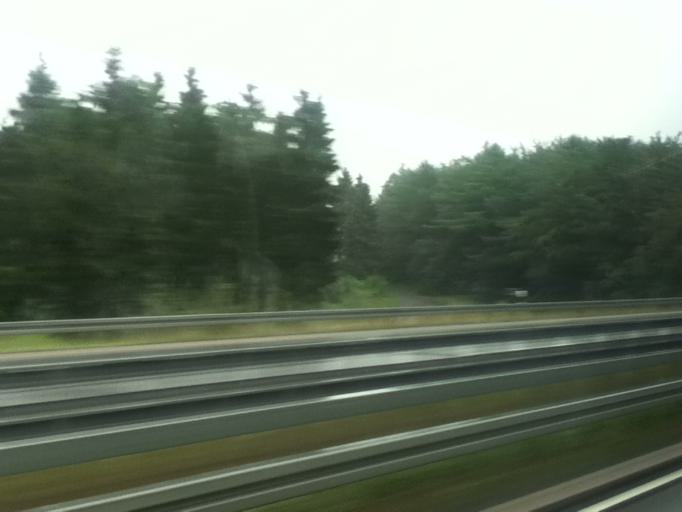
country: DE
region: North Rhine-Westphalia
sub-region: Regierungsbezirk Arnsberg
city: Wenden
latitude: 50.9910
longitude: 7.9080
